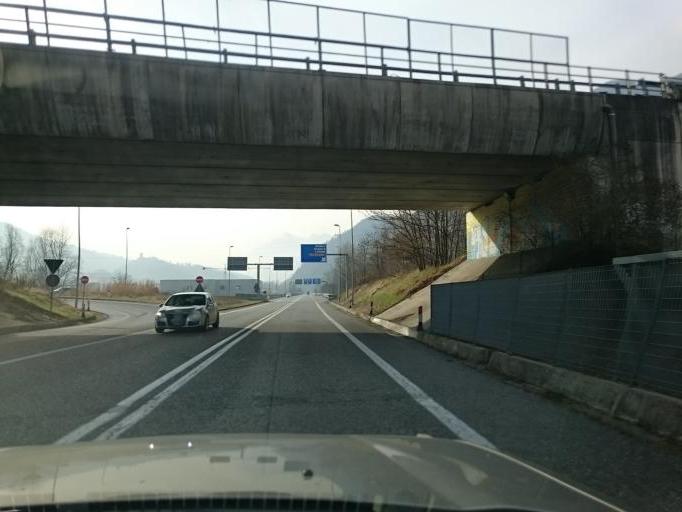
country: IT
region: Lombardy
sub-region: Provincia di Brescia
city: Breno
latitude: 45.9653
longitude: 10.3134
